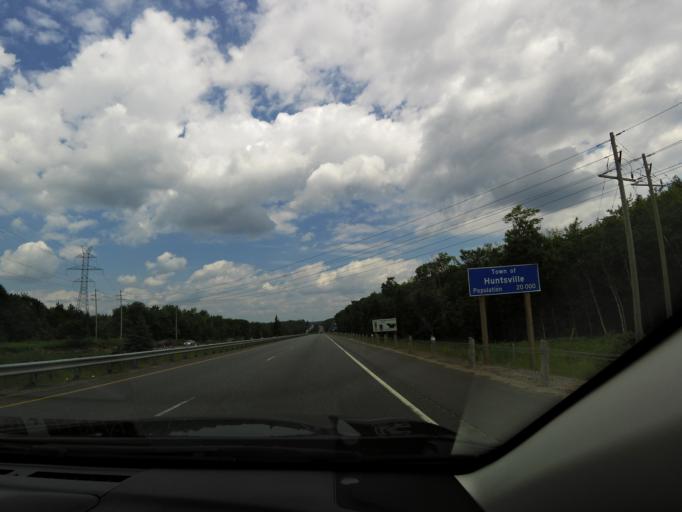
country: CA
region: Ontario
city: Bracebridge
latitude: 45.1587
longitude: -79.3112
